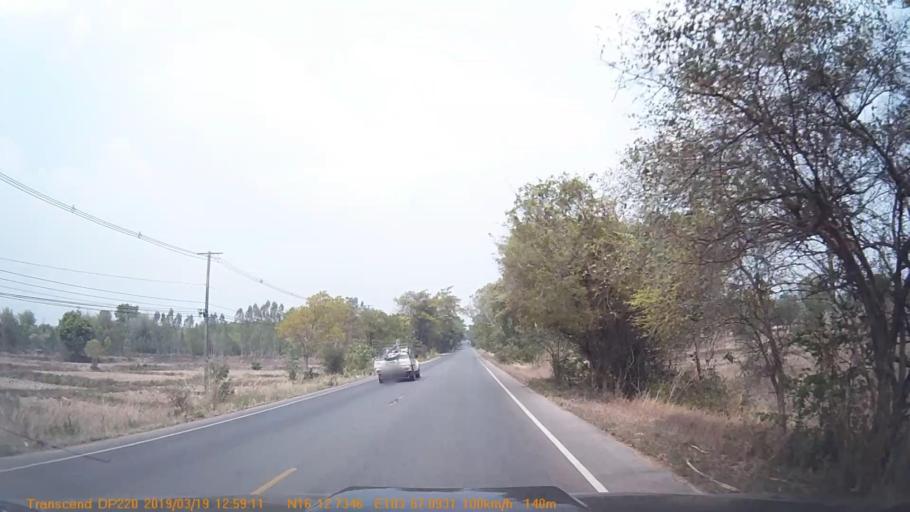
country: TH
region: Roi Et
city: Waeng
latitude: 16.2125
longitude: 103.9516
